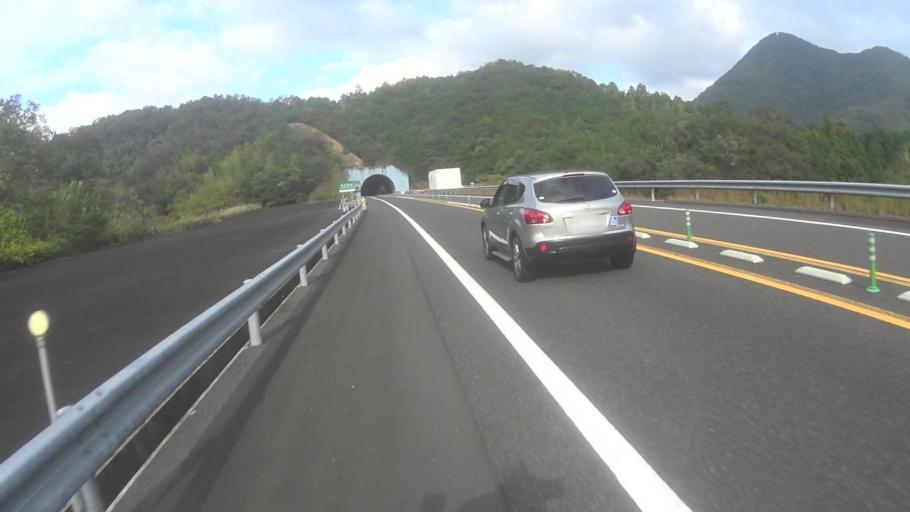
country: JP
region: Kyoto
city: Miyazu
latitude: 35.4361
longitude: 135.2011
